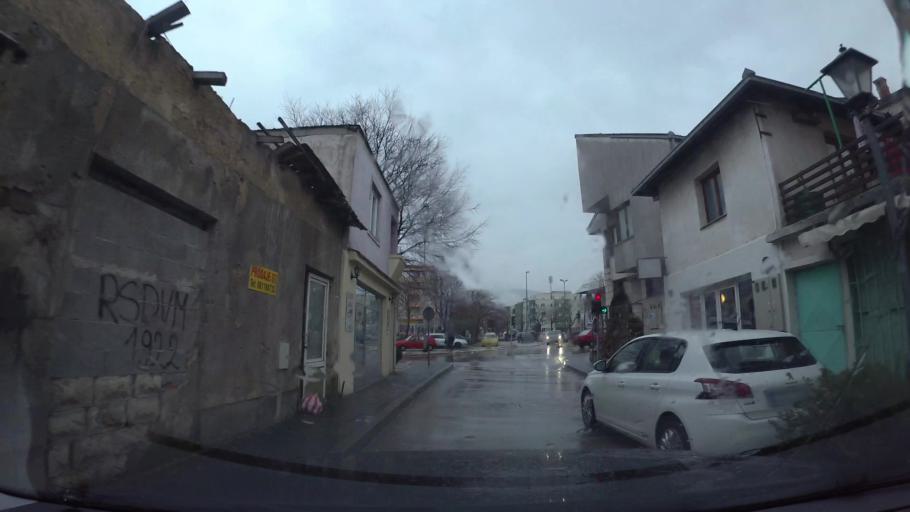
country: BA
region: Federation of Bosnia and Herzegovina
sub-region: Hercegovacko-Bosanski Kanton
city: Mostar
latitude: 43.3480
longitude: 17.8125
